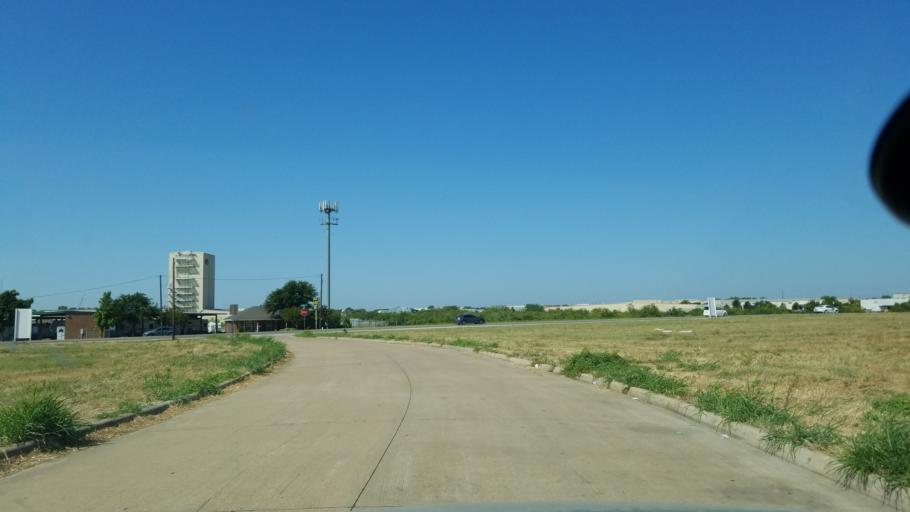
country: US
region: Texas
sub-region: Tarrant County
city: Mansfield
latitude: 32.5537
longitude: -97.1347
